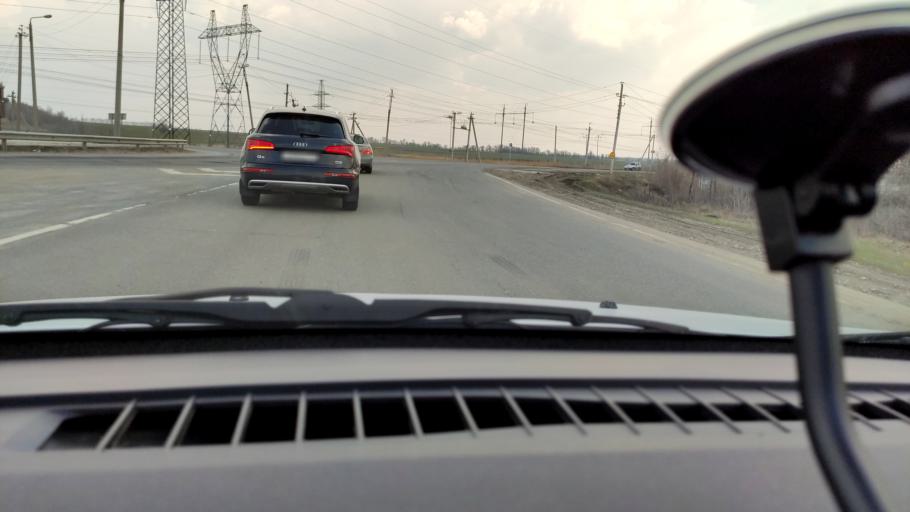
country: RU
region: Samara
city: Dubovyy Umet
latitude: 53.0627
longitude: 50.3758
